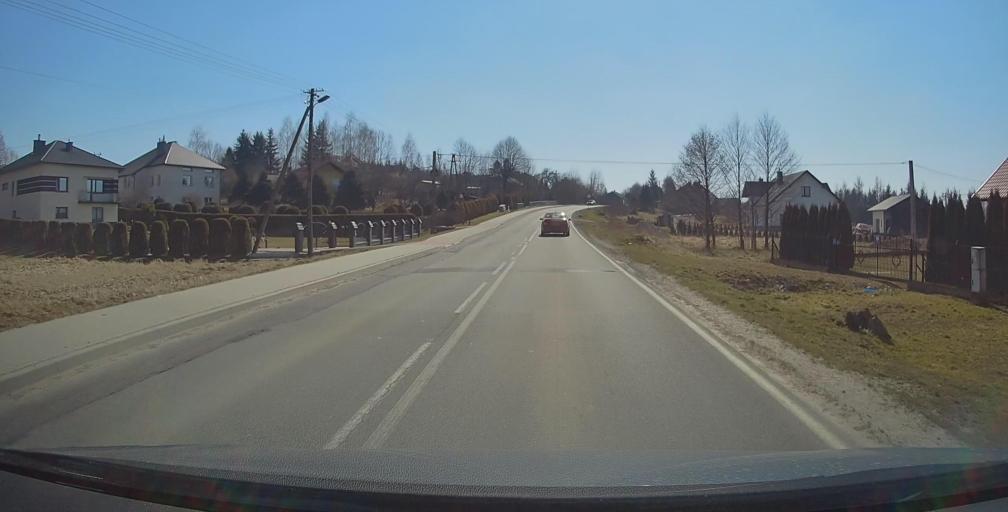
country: PL
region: Subcarpathian Voivodeship
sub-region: Powiat rzeszowski
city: Chmielnik
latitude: 49.9491
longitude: 22.1010
